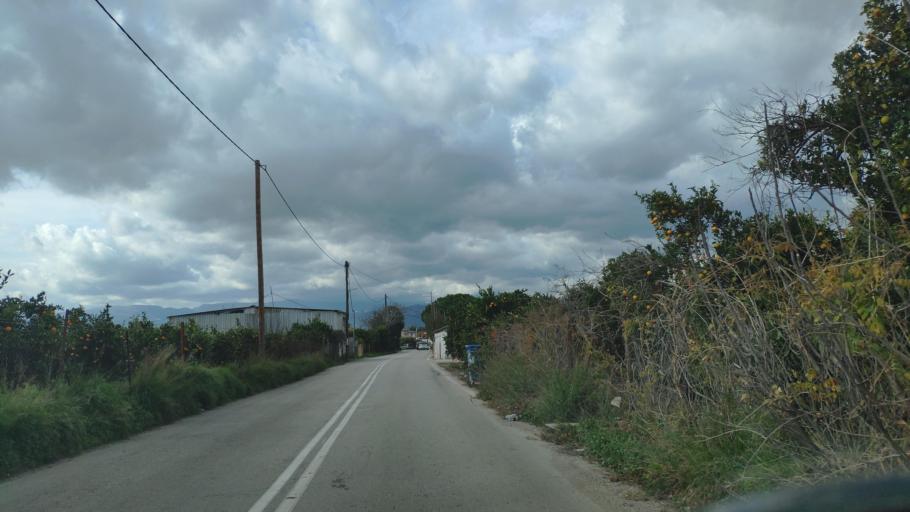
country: GR
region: Peloponnese
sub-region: Nomos Argolidos
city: Nea Tirins
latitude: 37.6083
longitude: 22.8021
